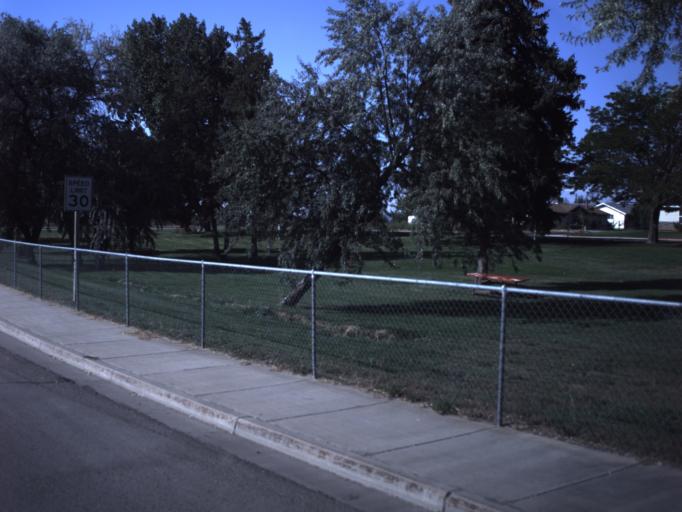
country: US
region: Utah
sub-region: San Juan County
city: Blanding
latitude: 37.6180
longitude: -109.4781
